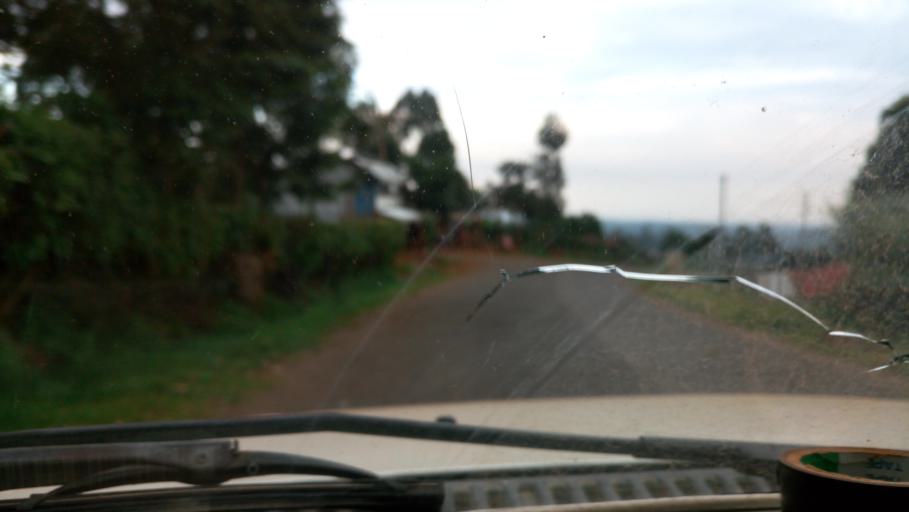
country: KE
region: Murang'a District
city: Kangema
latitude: -0.6498
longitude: 36.8835
